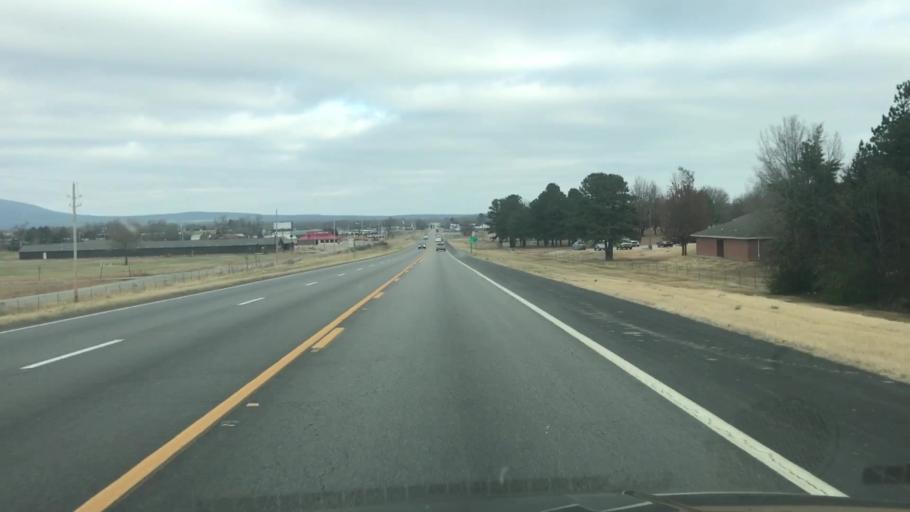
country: US
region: Arkansas
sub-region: Scott County
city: Waldron
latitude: 34.8927
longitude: -94.1076
